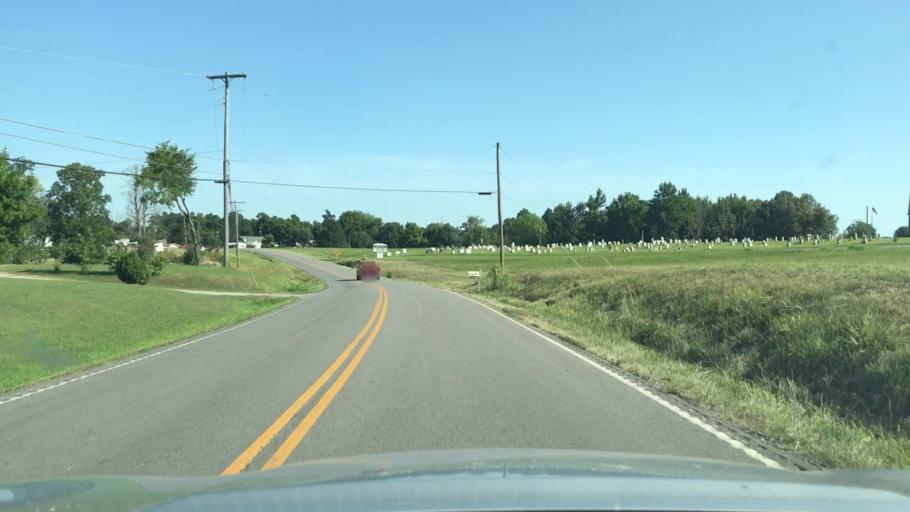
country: US
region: Kentucky
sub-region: Muhlenberg County
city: Greenville
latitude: 37.1789
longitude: -87.1526
